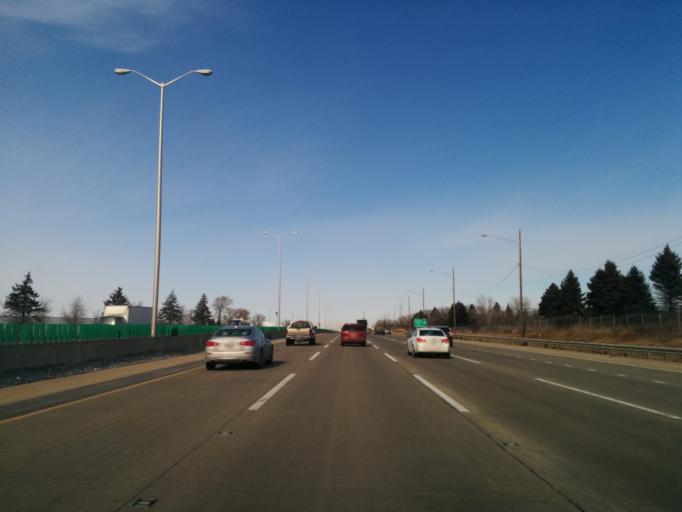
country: US
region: Illinois
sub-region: Lake County
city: Gurnee
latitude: 42.3702
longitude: -87.9420
